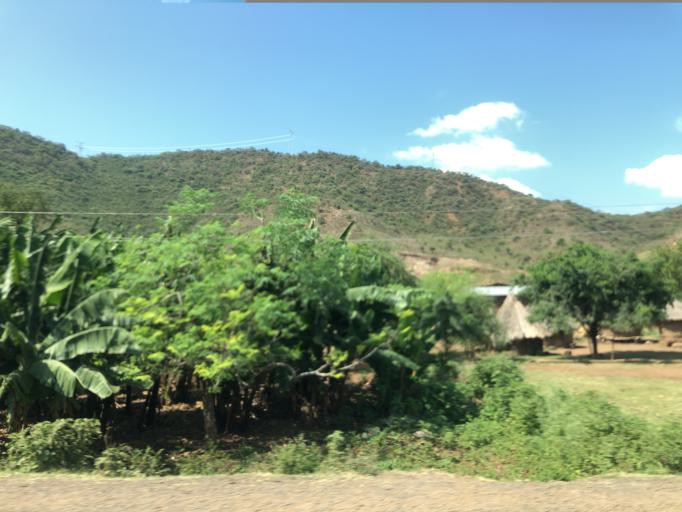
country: ET
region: Southern Nations, Nationalities, and People's Region
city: Gidole
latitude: 5.8170
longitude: 37.4566
